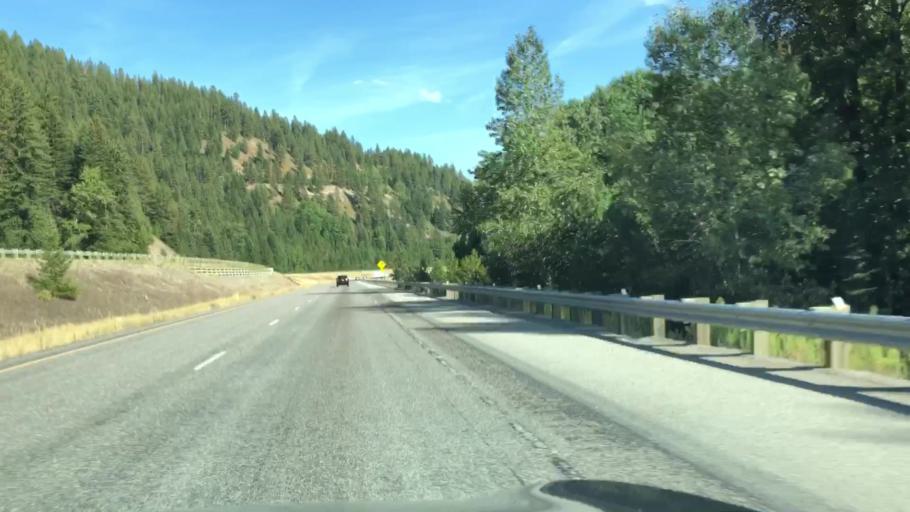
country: US
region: Montana
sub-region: Sanders County
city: Thompson Falls
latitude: 47.4044
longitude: -115.4828
